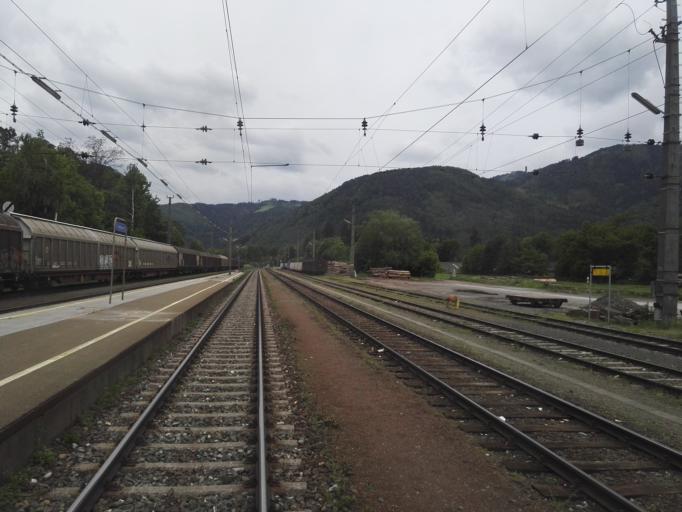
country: AT
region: Styria
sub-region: Politischer Bezirk Graz-Umgebung
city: Frohnleiten
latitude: 47.2658
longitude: 15.3261
